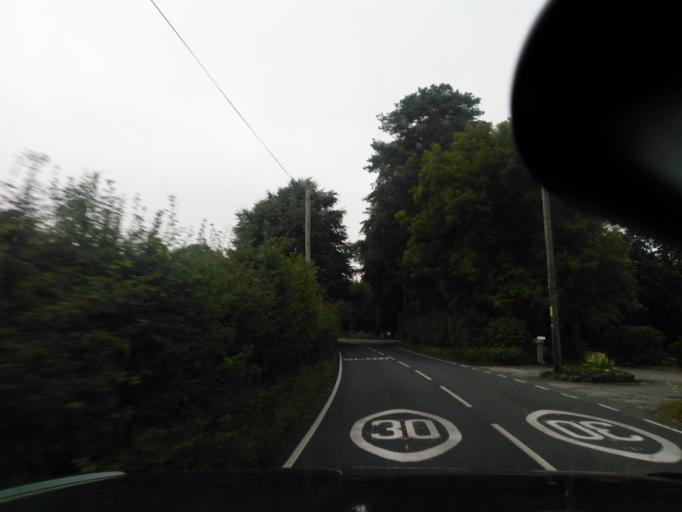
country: GB
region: England
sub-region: Dorset
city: Shaftesbury
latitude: 50.9651
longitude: -2.1890
